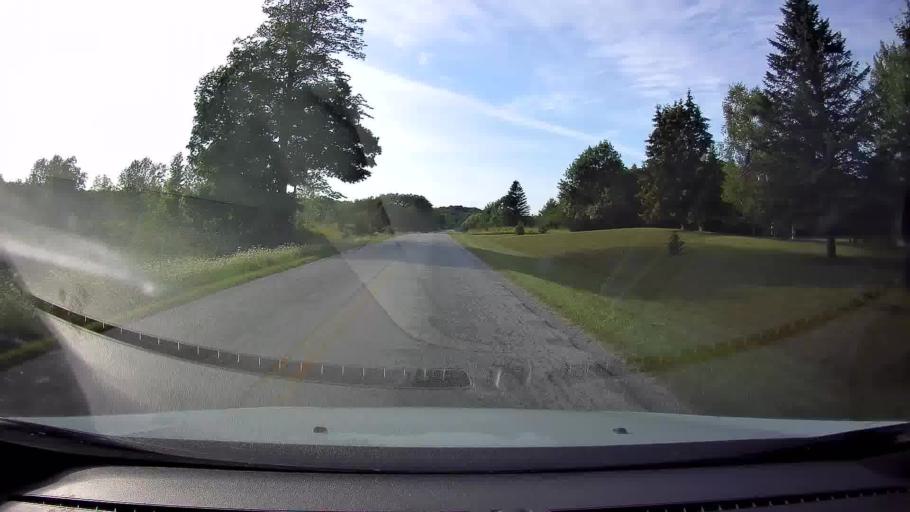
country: US
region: Wisconsin
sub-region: Door County
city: Sturgeon Bay
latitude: 45.1743
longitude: -87.1384
